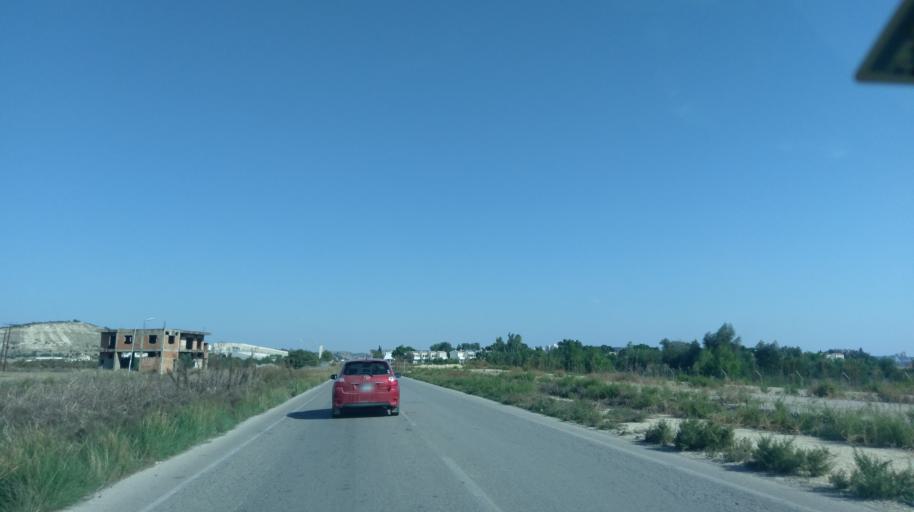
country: CY
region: Ammochostos
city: Trikomo
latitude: 35.3225
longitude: 33.9631
